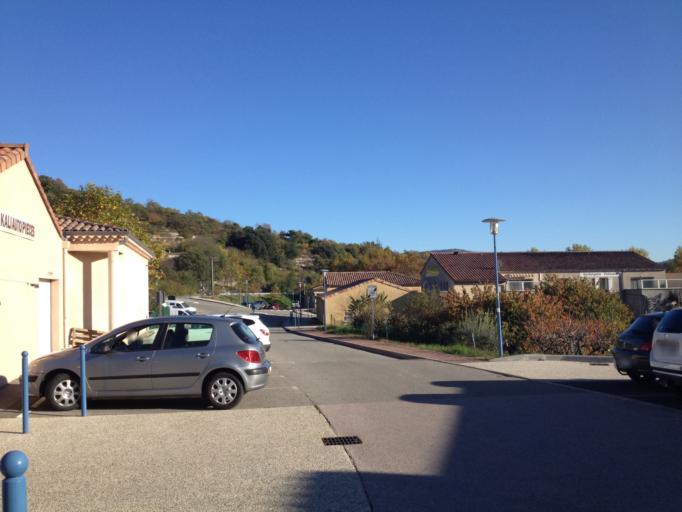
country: FR
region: Rhone-Alpes
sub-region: Departement de l'Ardeche
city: Alissas
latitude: 44.7147
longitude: 4.6316
